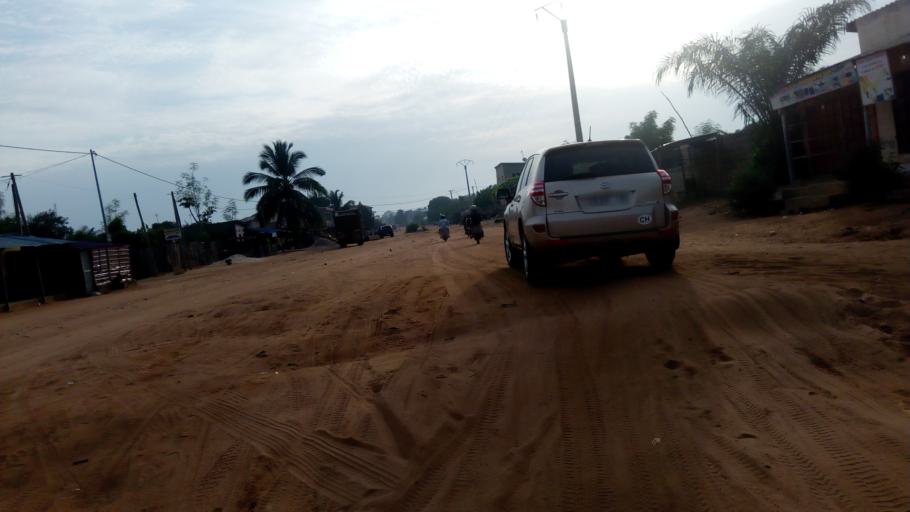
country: TG
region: Maritime
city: Lome
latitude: 6.1787
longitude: 1.1484
